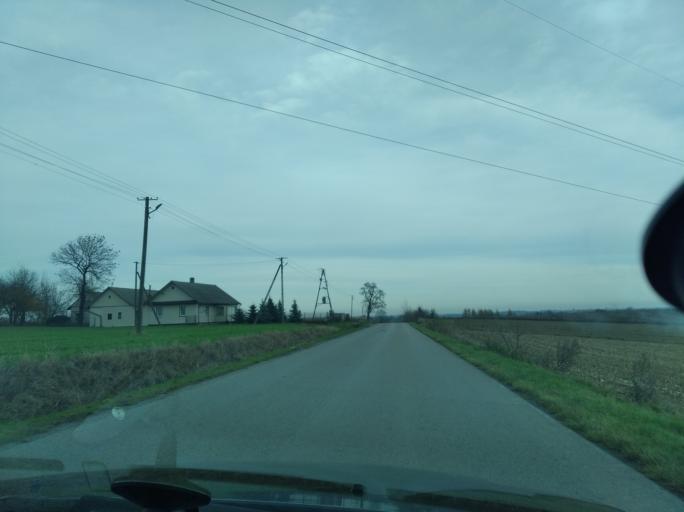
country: PL
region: Subcarpathian Voivodeship
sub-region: Powiat przeworski
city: Debow
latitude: 50.0390
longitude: 22.4267
